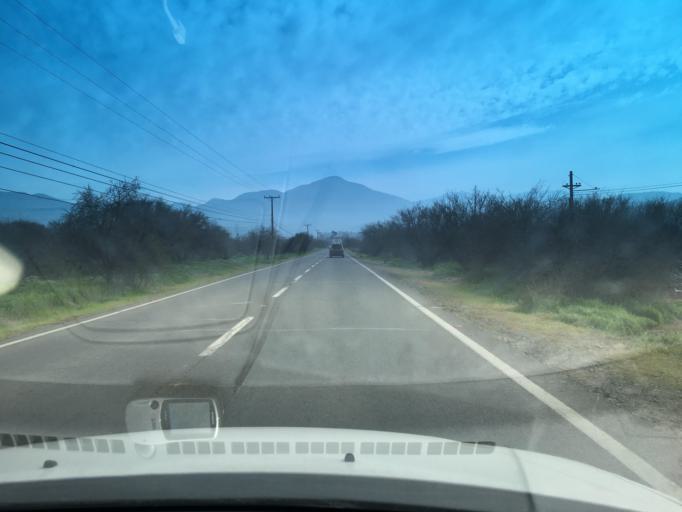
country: CL
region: Santiago Metropolitan
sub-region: Provincia de Chacabuco
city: Lampa
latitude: -33.1296
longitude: -70.9216
